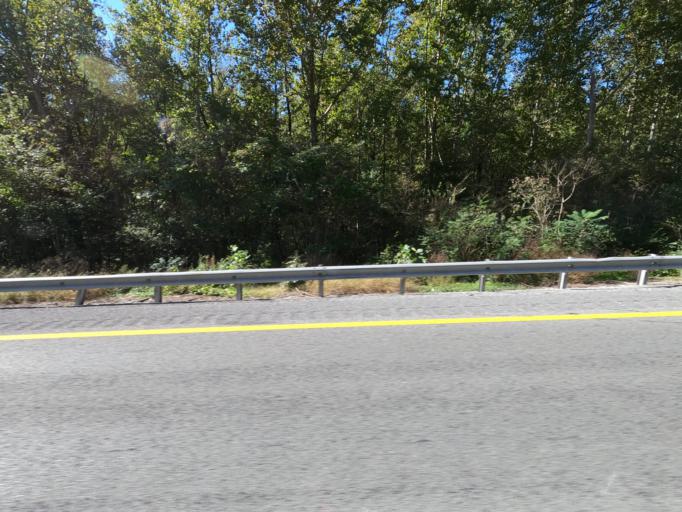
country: US
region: Tennessee
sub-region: Cheatham County
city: Pegram
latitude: 36.0848
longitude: -87.0464
